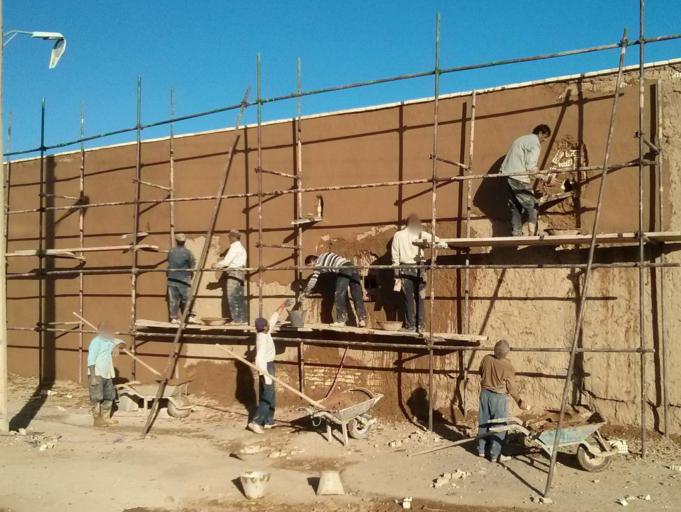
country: IR
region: Isfahan
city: Na'in
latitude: 32.2784
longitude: 52.9088
